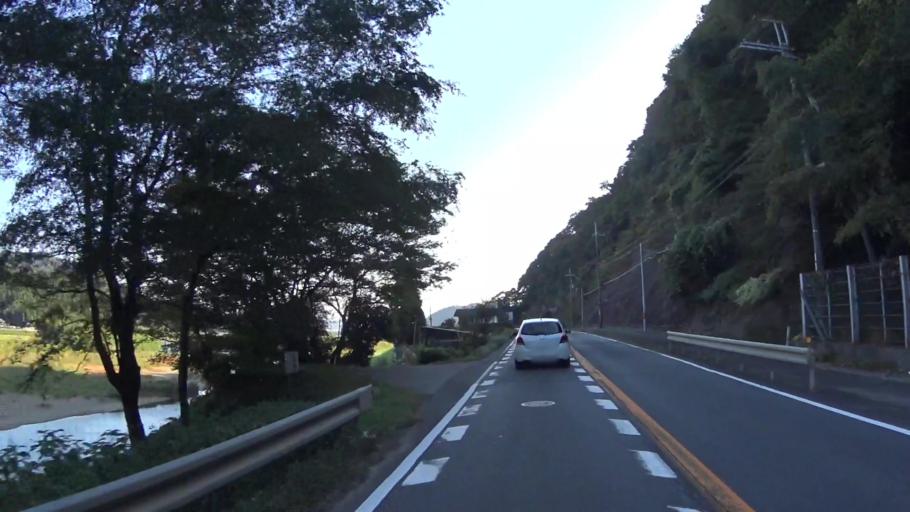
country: JP
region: Kyoto
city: Fukuchiyama
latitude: 35.3483
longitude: 135.1077
